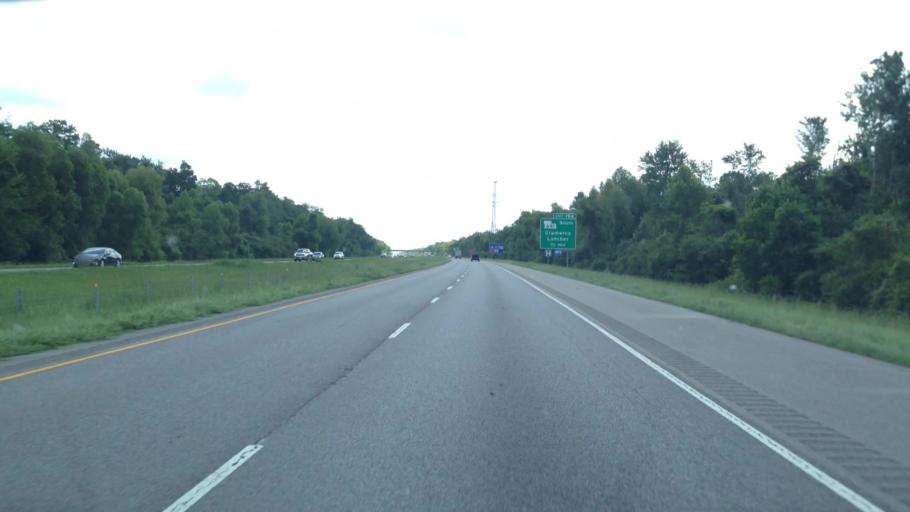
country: US
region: Louisiana
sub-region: Saint James Parish
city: Gramercy
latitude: 30.1248
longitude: -90.6956
